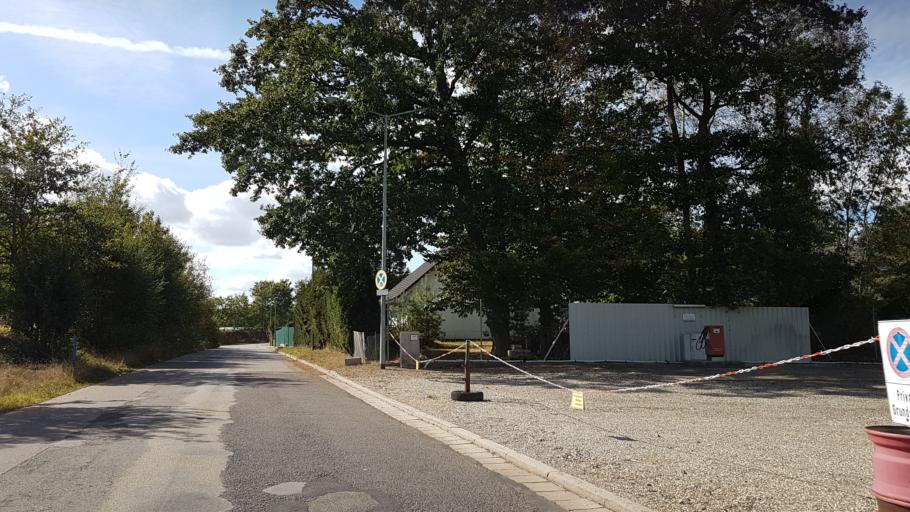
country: DE
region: Saarland
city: Kirkel
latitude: 49.2895
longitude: 7.2202
